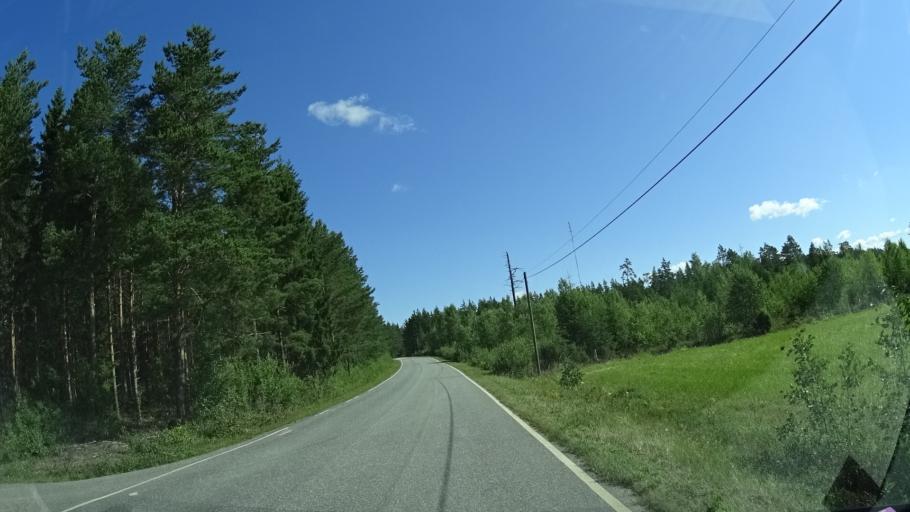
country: FI
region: Varsinais-Suomi
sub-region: Turku
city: Velkua
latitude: 60.4743
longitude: 21.7151
